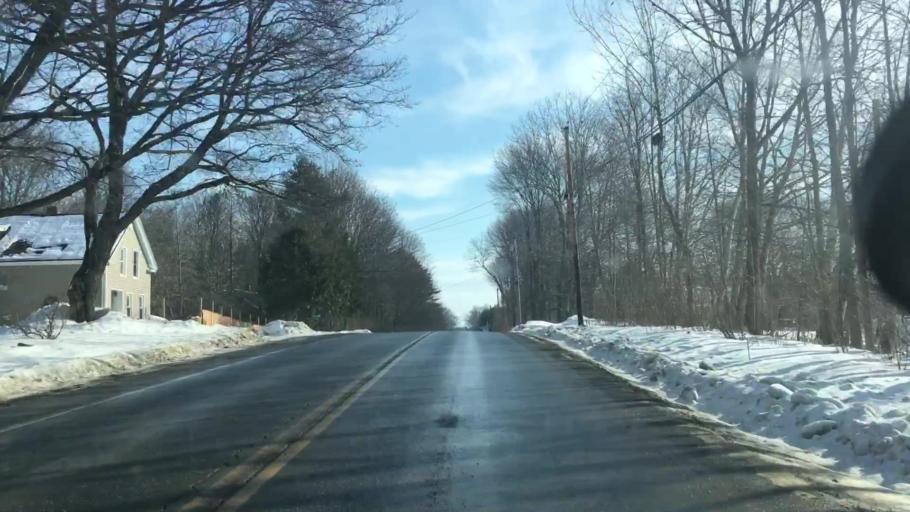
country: US
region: Maine
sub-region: Penobscot County
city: Bangor
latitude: 44.8488
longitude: -68.8402
